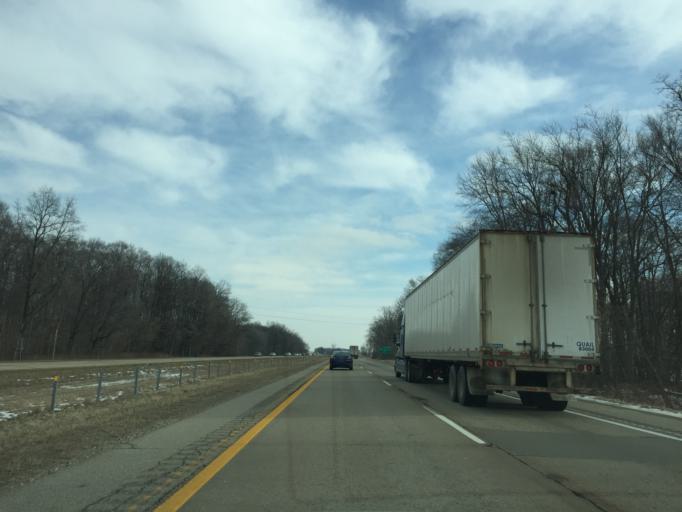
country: US
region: Michigan
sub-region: Ionia County
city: Saranac
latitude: 42.8791
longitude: -85.1622
